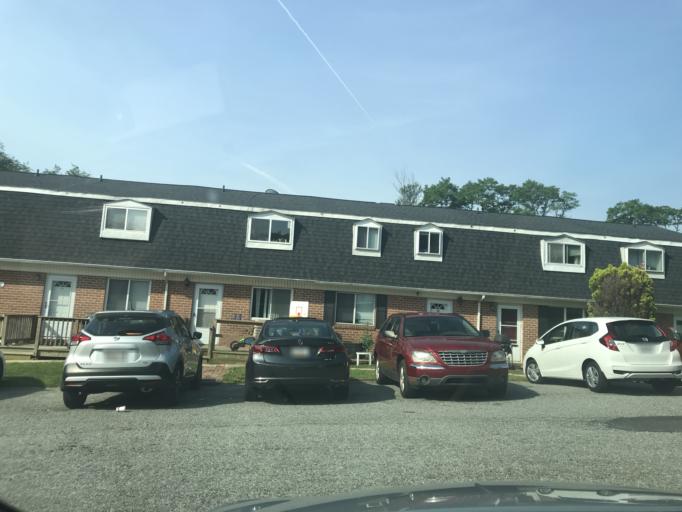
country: US
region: Maryland
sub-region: Harford County
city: Bel Air North
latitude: 39.5706
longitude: -76.3646
